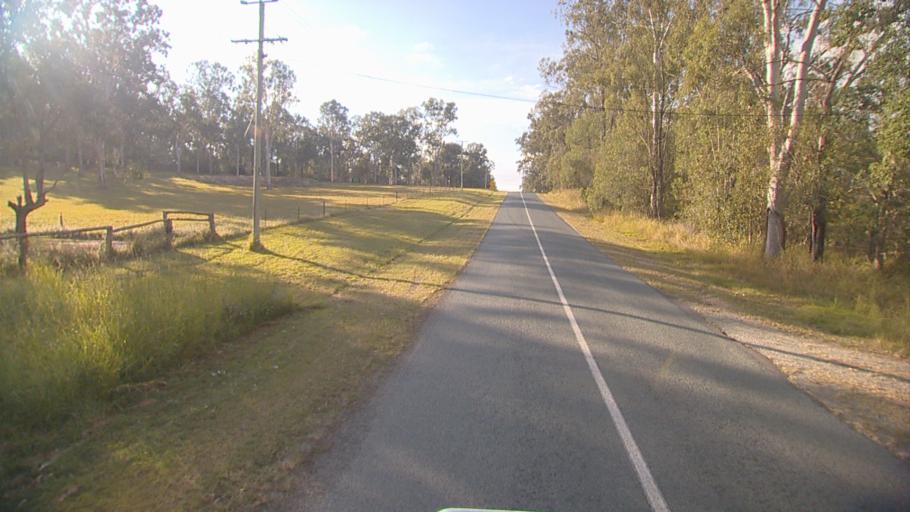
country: AU
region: Queensland
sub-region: Gold Coast
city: Ormeau Hills
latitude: -27.8362
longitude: 153.1689
